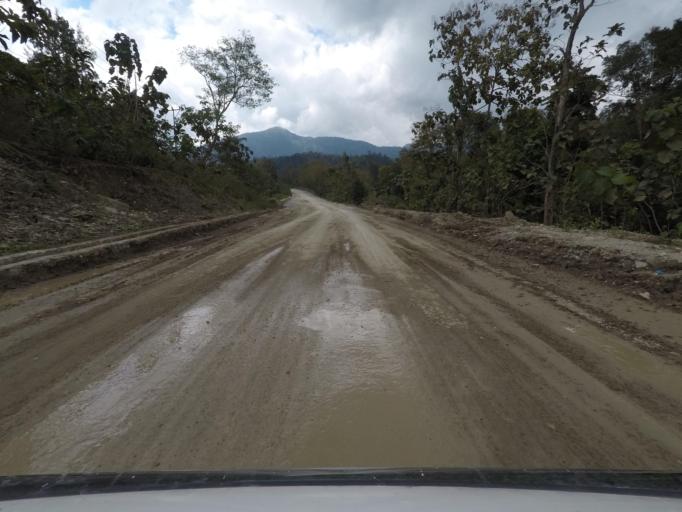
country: TL
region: Viqueque
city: Viqueque
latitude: -8.8160
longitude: 126.3806
